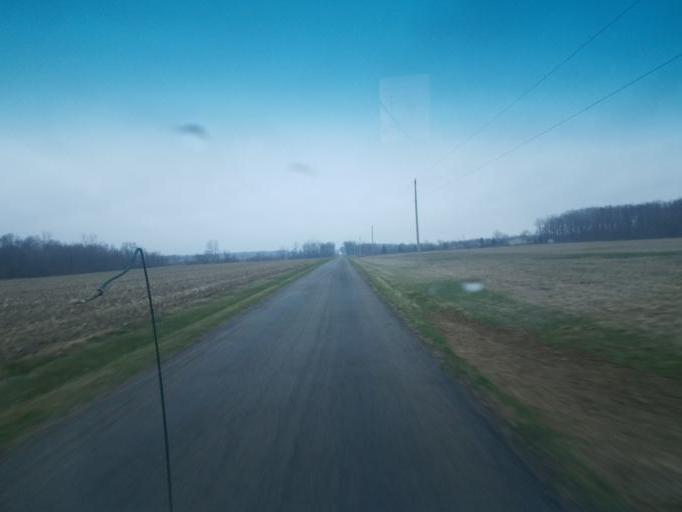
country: US
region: Ohio
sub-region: Defiance County
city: Hicksville
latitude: 41.3391
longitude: -84.7625
